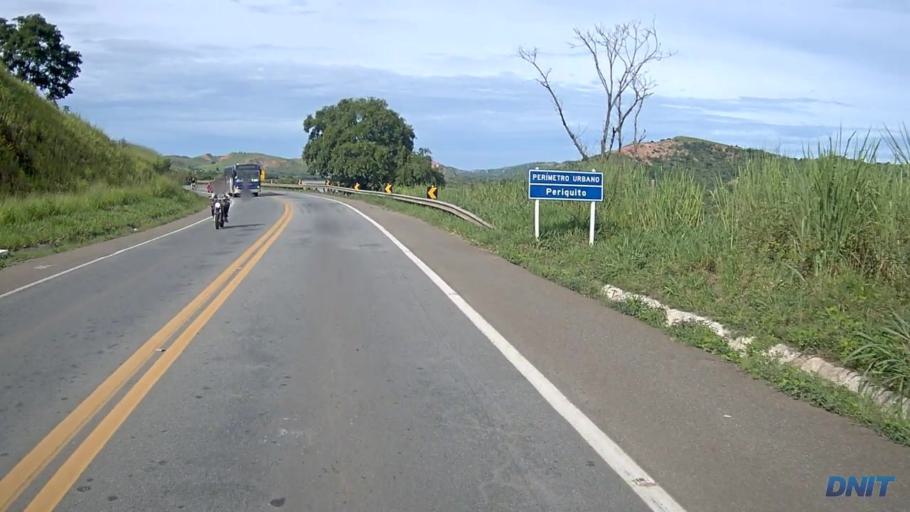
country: BR
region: Minas Gerais
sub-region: Belo Oriente
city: Belo Oriente
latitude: -19.1604
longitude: -42.2390
